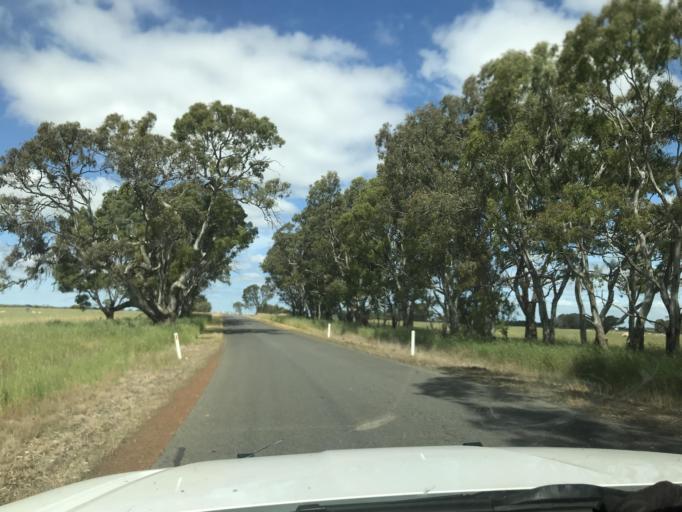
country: AU
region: South Australia
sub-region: Naracoorte and Lucindale
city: Naracoorte
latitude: -36.9922
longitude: 141.2865
